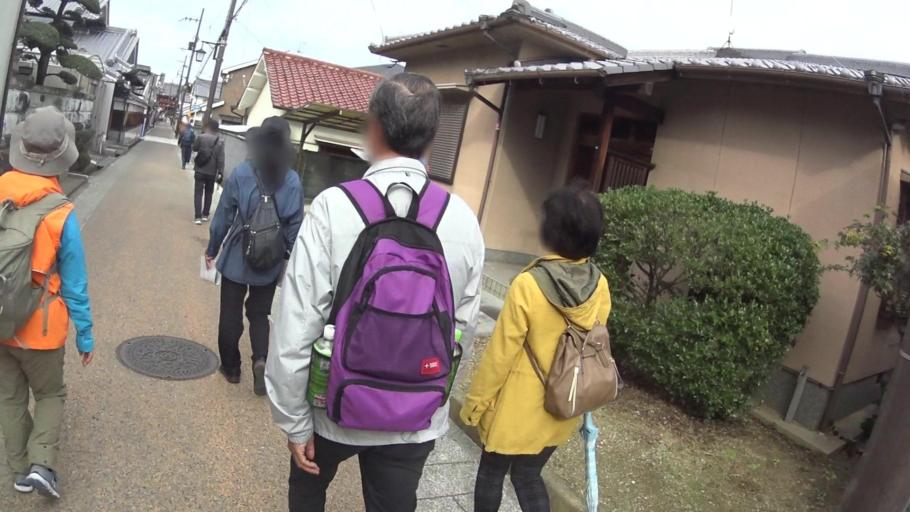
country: JP
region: Osaka
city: Kashihara
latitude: 34.5675
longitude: 135.5967
